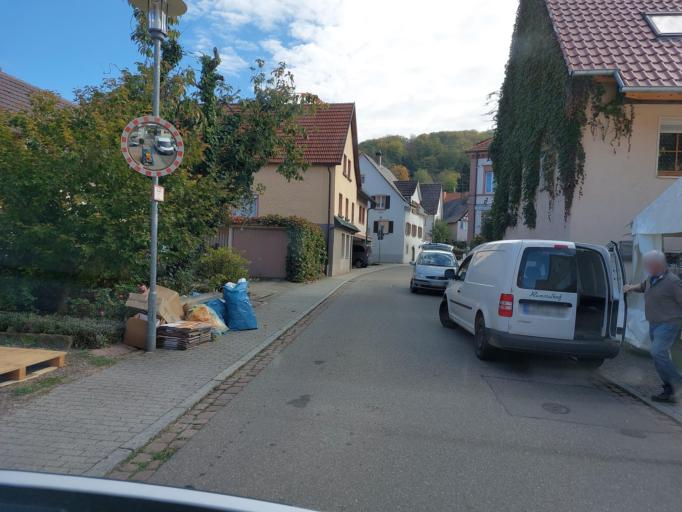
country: DE
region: Baden-Wuerttemberg
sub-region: Freiburg Region
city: Malterdingen
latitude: 48.1636
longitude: 7.8306
